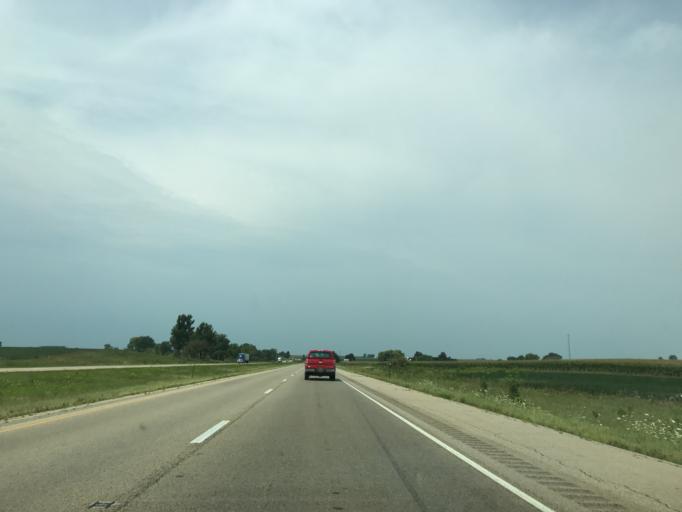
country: US
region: Illinois
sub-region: Bureau County
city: Depue
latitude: 41.3921
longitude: -89.2890
